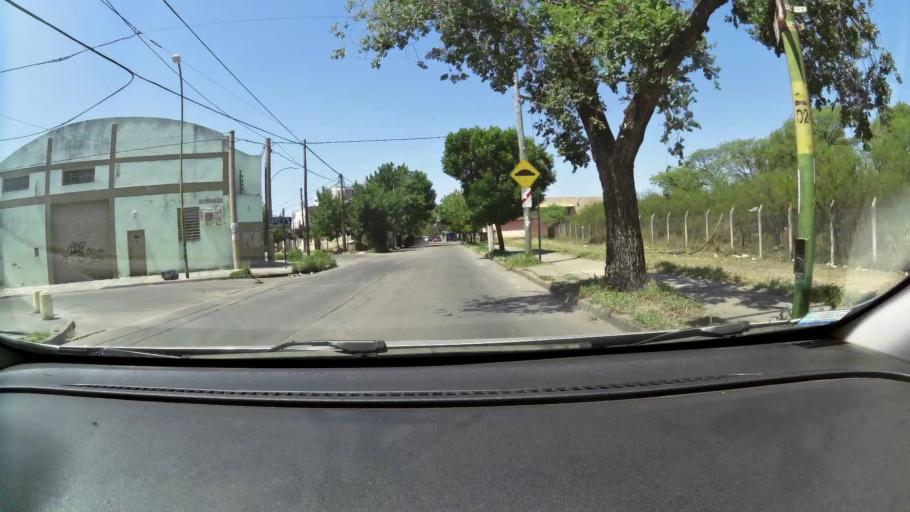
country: AR
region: Cordoba
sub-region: Departamento de Capital
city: Cordoba
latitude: -31.3898
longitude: -64.1566
